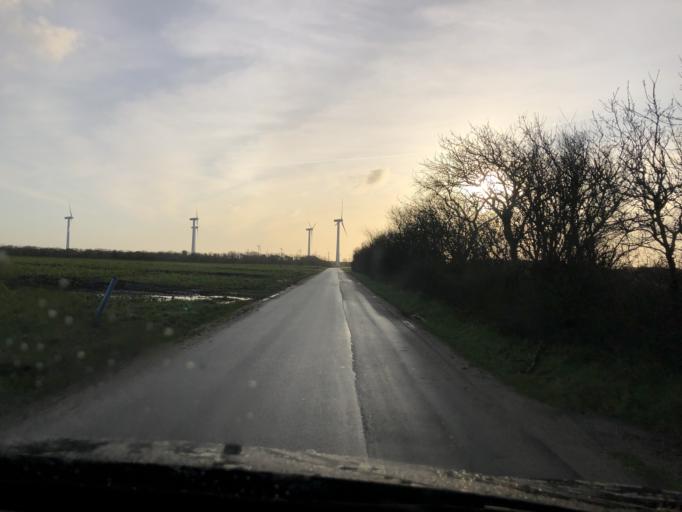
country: DK
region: Central Jutland
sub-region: Ringkobing-Skjern Kommune
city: Skjern
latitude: 55.8692
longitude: 8.3584
